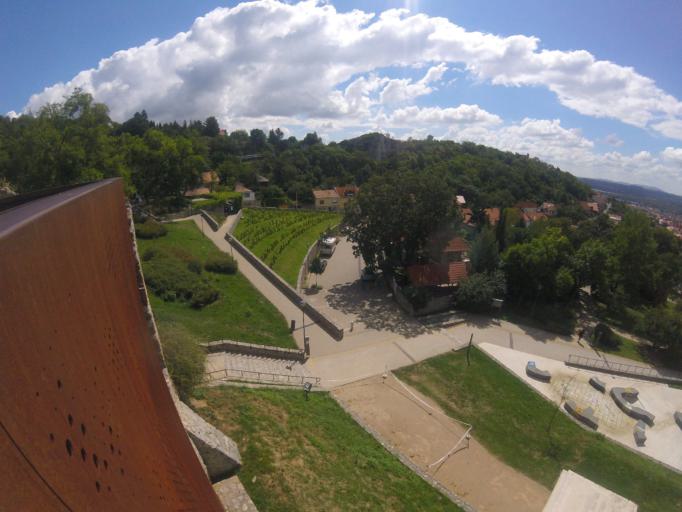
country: HU
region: Baranya
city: Pecs
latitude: 46.0872
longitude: 18.2357
